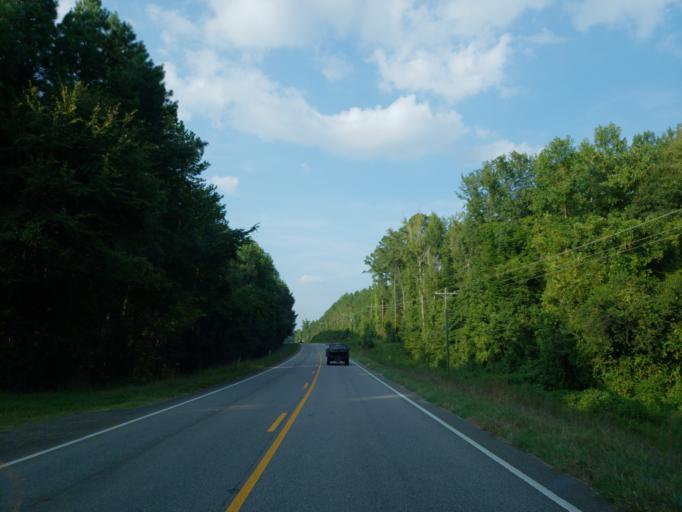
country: US
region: Alabama
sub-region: Greene County
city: Eutaw
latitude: 32.9390
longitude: -87.8081
